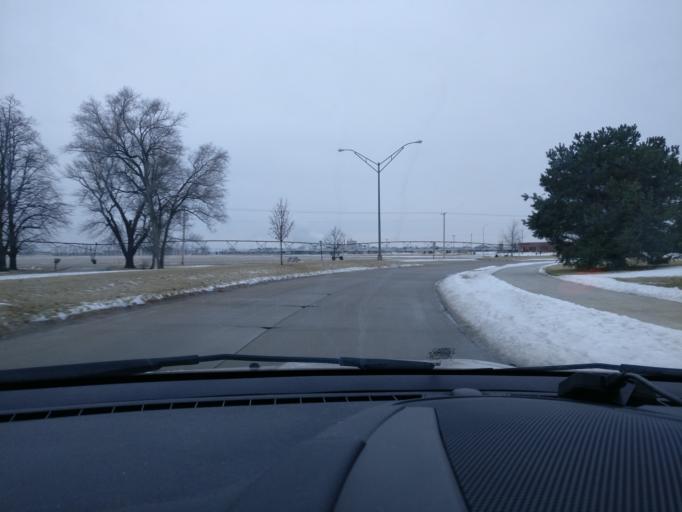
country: US
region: Nebraska
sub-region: Dodge County
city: Fremont
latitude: 41.4450
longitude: -96.4522
